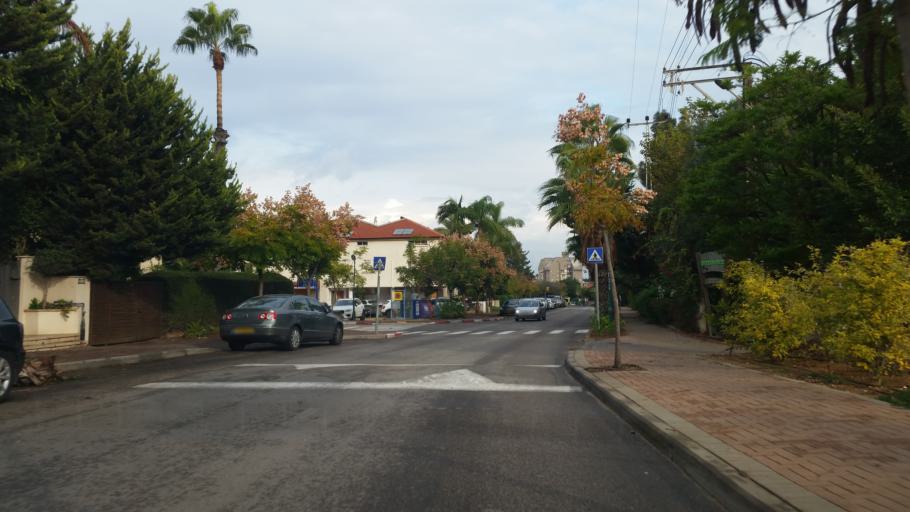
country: IL
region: Tel Aviv
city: Ramat HaSharon
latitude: 32.1547
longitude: 34.8474
